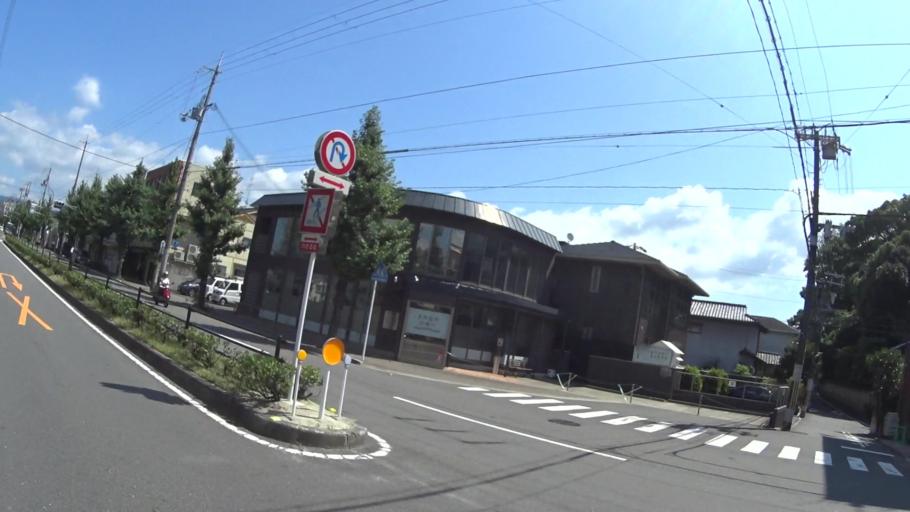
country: JP
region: Kyoto
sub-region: Kyoto-shi
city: Kamigyo-ku
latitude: 35.0397
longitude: 135.7708
